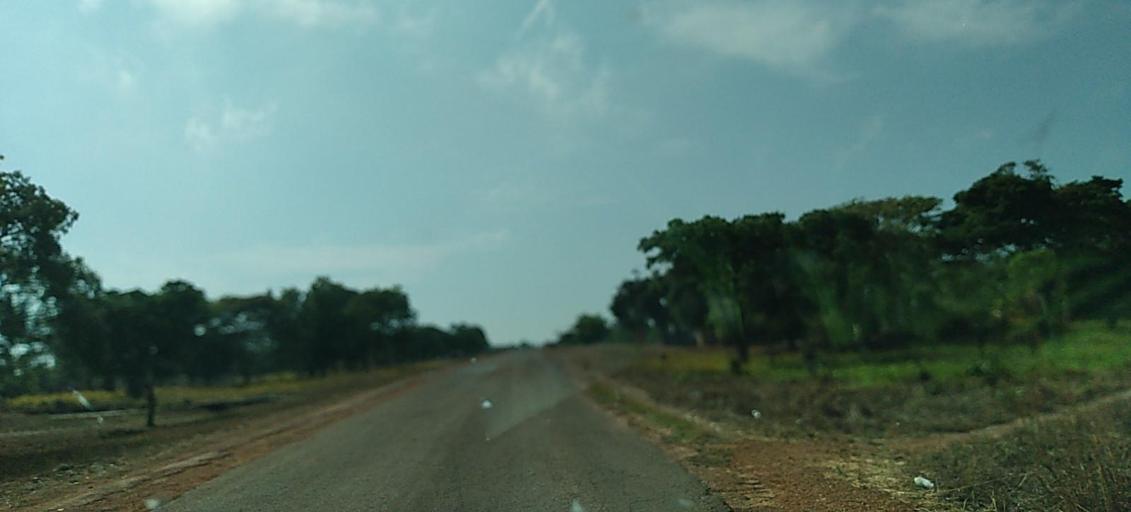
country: ZM
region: North-Western
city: Mwinilunga
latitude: -11.7726
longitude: 25.0134
